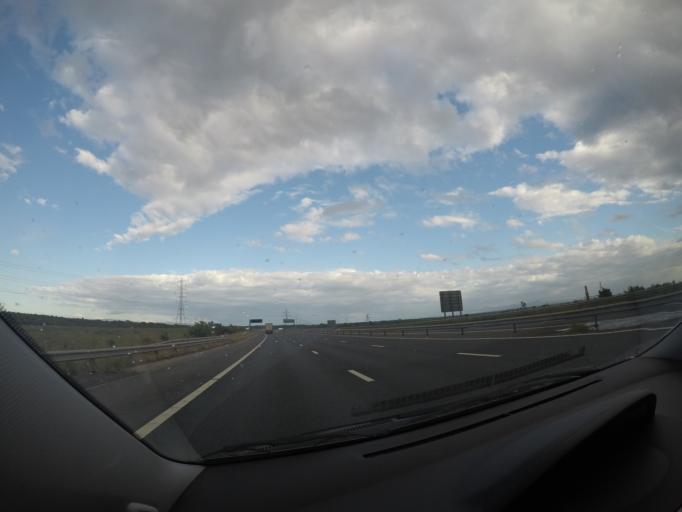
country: GB
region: Scotland
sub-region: Dumfries and Galloway
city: Gretna
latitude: 54.9877
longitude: -3.0383
